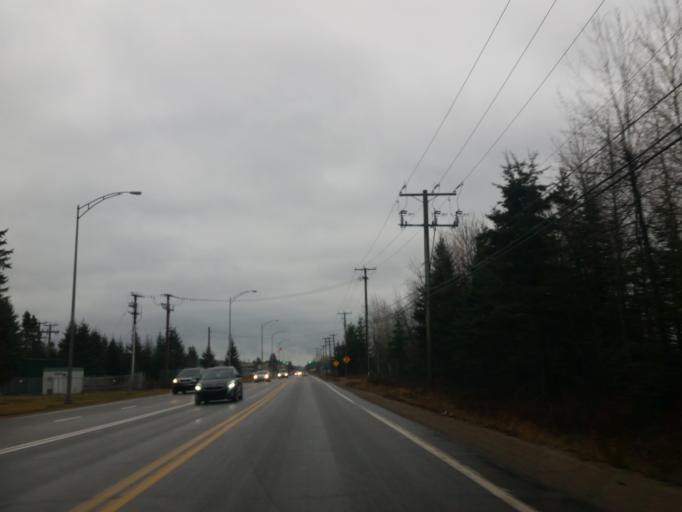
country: CA
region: Quebec
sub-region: Capitale-Nationale
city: Shannon
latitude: 46.8843
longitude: -71.4873
